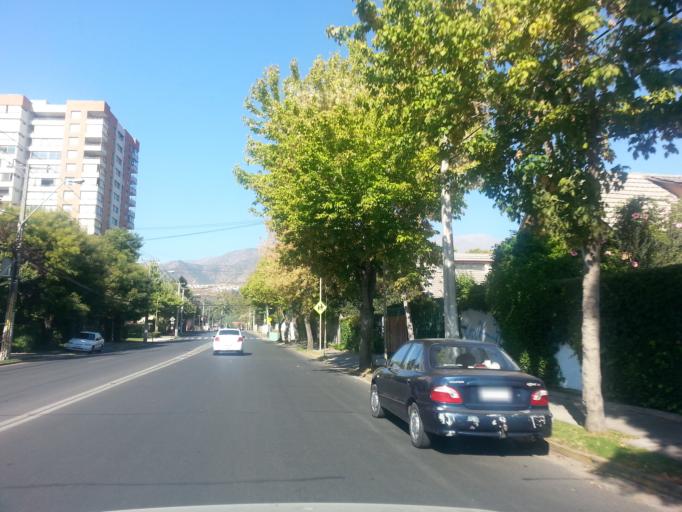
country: CL
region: Santiago Metropolitan
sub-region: Provincia de Santiago
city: Villa Presidente Frei, Nunoa, Santiago, Chile
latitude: -33.4242
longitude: -70.5412
